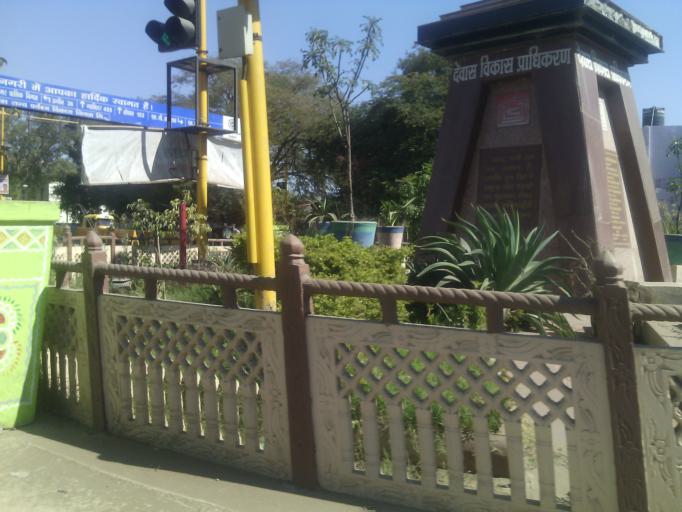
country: IN
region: Madhya Pradesh
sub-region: Dewas
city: Dewas
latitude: 22.9670
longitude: 76.0508
